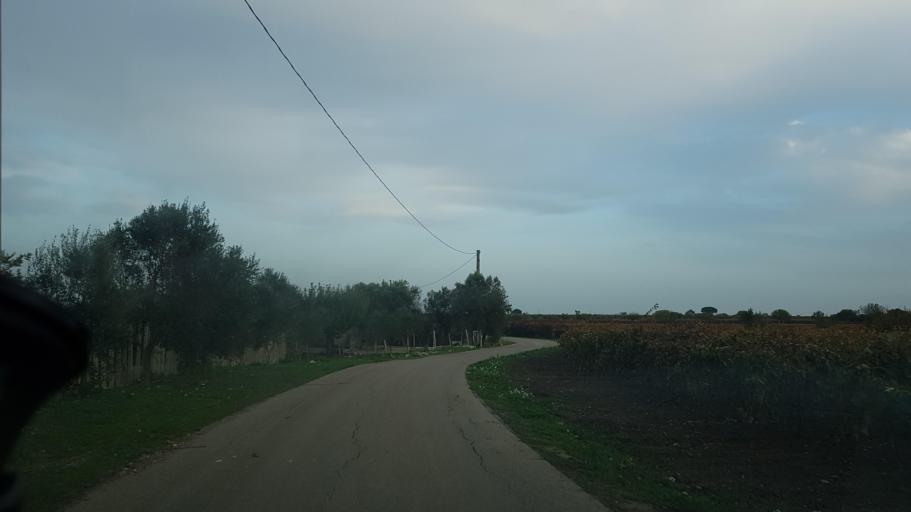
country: IT
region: Apulia
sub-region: Provincia di Brindisi
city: San Pancrazio Salentino
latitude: 40.4215
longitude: 17.8575
